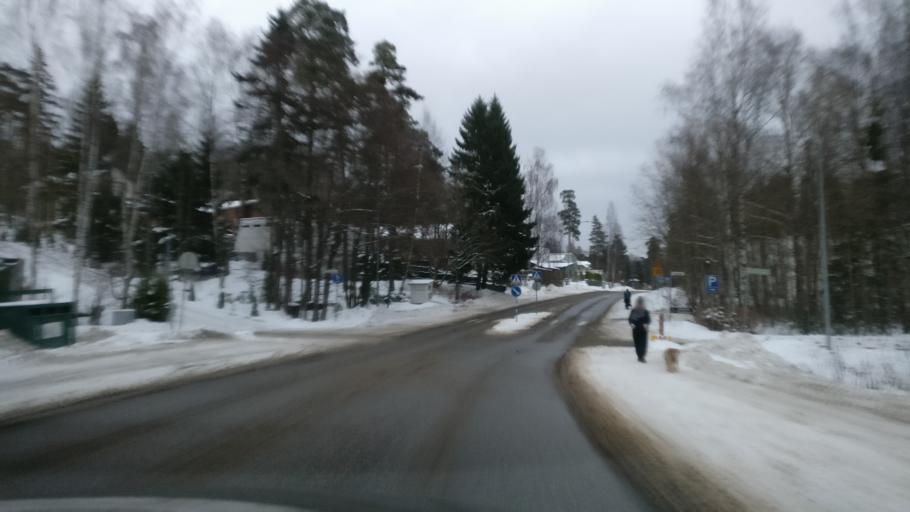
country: FI
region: Uusimaa
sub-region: Helsinki
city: Vantaa
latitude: 60.1648
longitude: 25.0729
